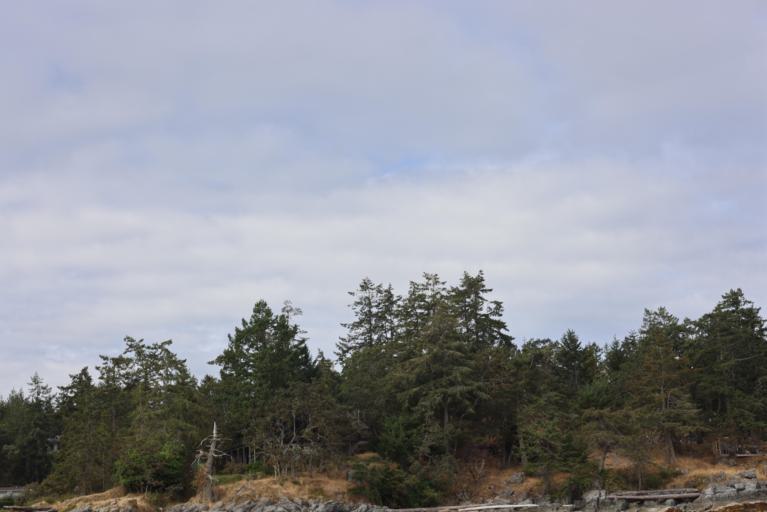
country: CA
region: British Columbia
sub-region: Regional District of Nanaimo
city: Parksville
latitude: 49.2841
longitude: -124.1286
